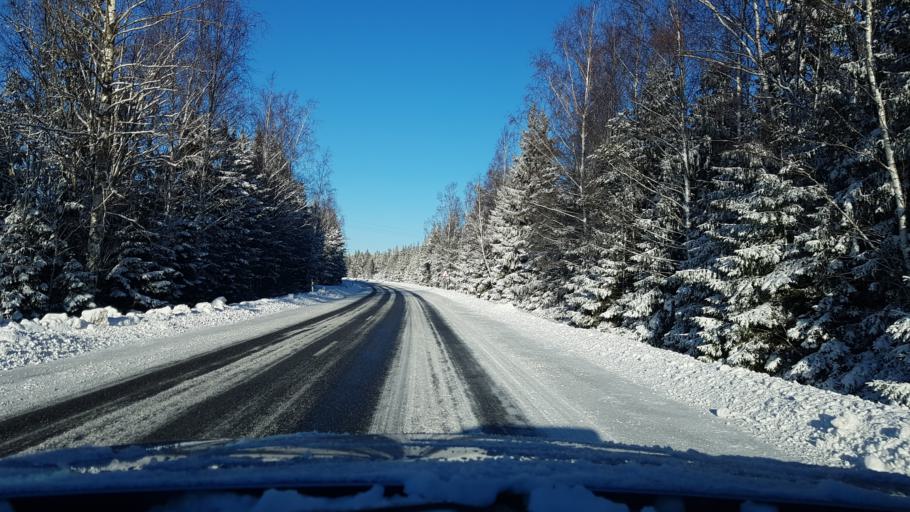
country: EE
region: Hiiumaa
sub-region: Kaerdla linn
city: Kardla
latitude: 58.9795
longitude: 22.8106
